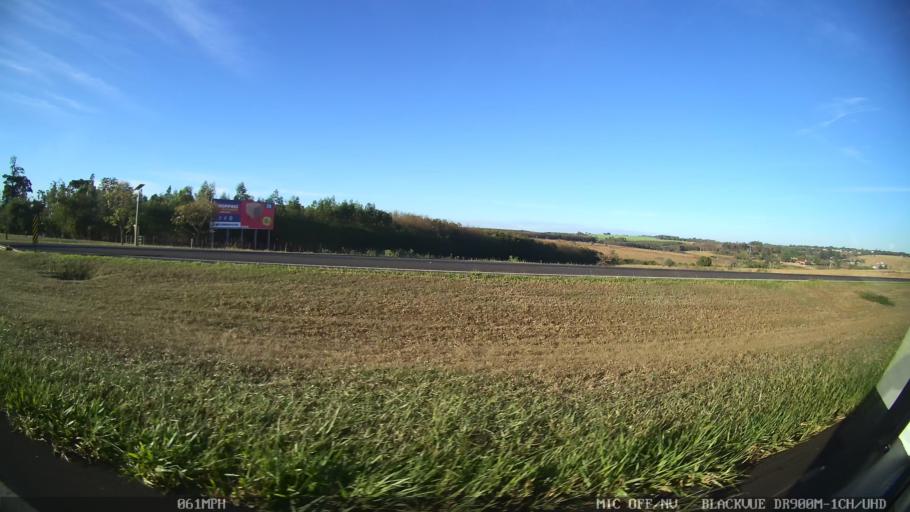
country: BR
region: Sao Paulo
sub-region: Sao Jose Do Rio Preto
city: Sao Jose do Rio Preto
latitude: -20.8885
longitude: -49.3103
